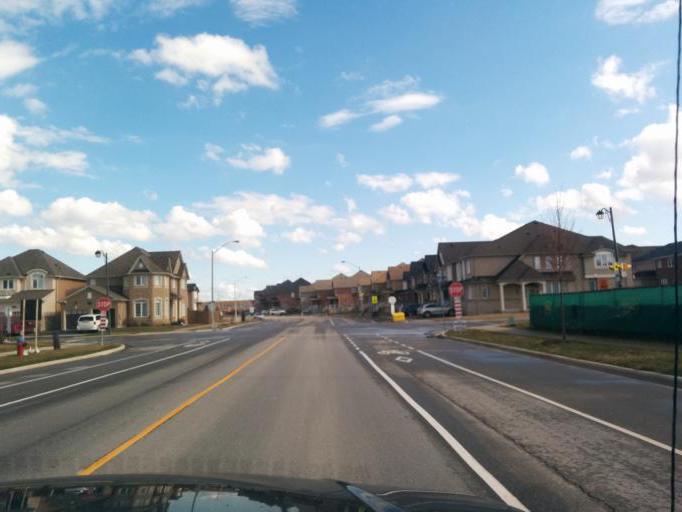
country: CA
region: Ontario
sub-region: Halton
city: Milton
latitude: 43.4980
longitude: -79.8655
